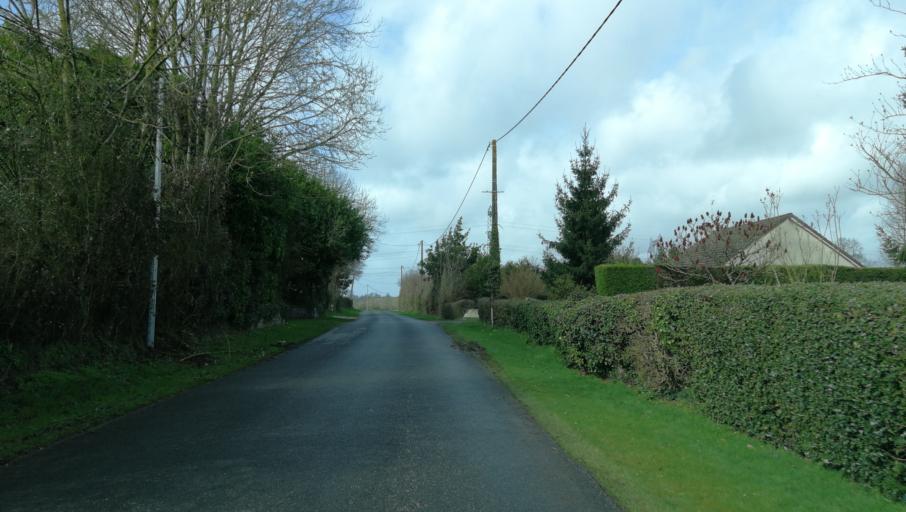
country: FR
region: Haute-Normandie
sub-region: Departement de l'Eure
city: Lieurey
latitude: 49.2394
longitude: 0.4796
